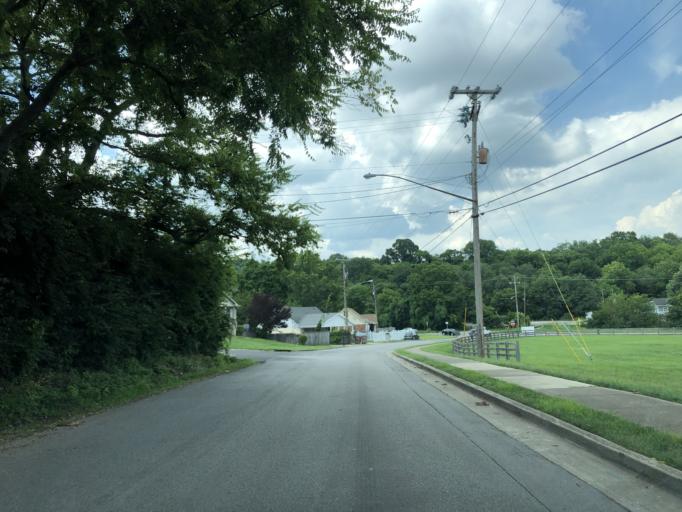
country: US
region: Tennessee
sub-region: Davidson County
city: Oak Hill
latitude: 36.1183
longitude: -86.7305
